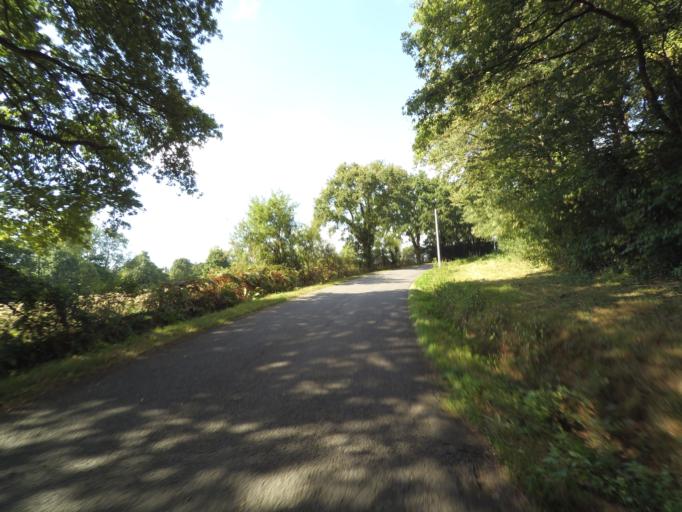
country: FR
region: Pays de la Loire
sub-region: Departement de la Loire-Atlantique
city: Vieillevigne
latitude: 46.9795
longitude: -1.4257
